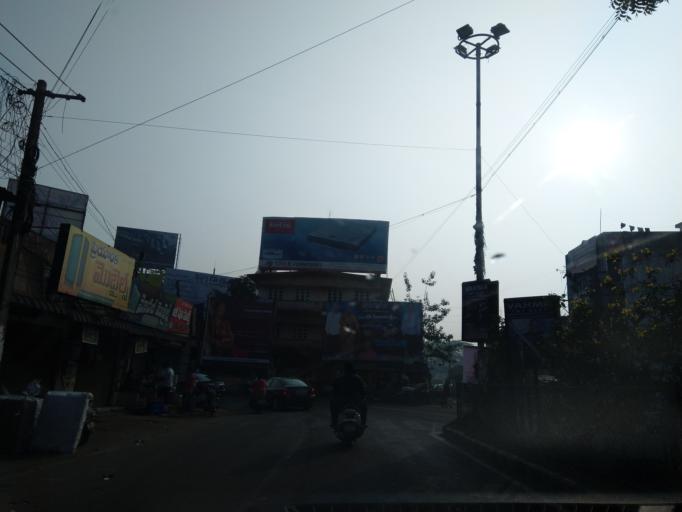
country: IN
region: Andhra Pradesh
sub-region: West Godavari
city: Bhimavaram
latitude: 16.5446
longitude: 81.5202
